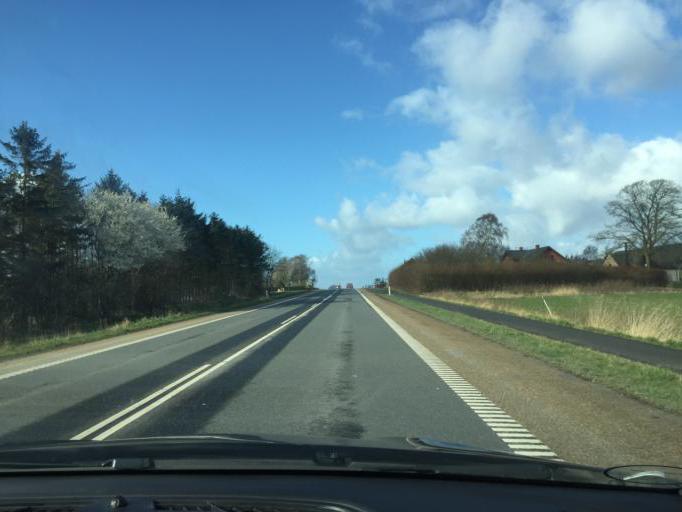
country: DK
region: South Denmark
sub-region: Middelfart Kommune
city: Norre Aby
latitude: 55.4813
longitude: 9.8402
